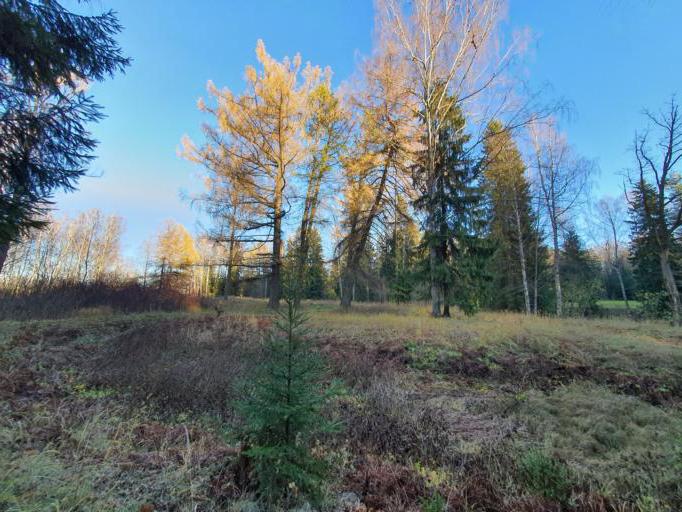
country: RU
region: St.-Petersburg
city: Tyarlevo
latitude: 59.6968
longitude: 30.4544
